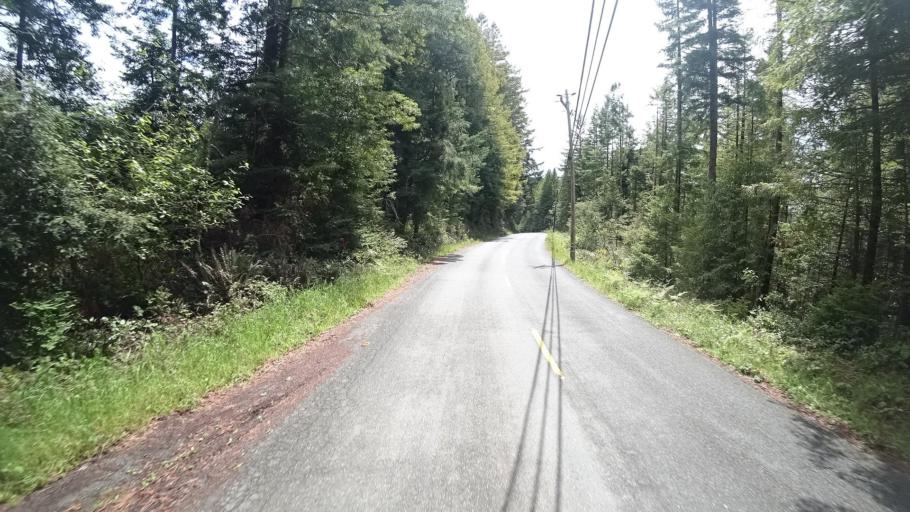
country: US
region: California
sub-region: Humboldt County
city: Bayside
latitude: 40.7944
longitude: -124.0255
